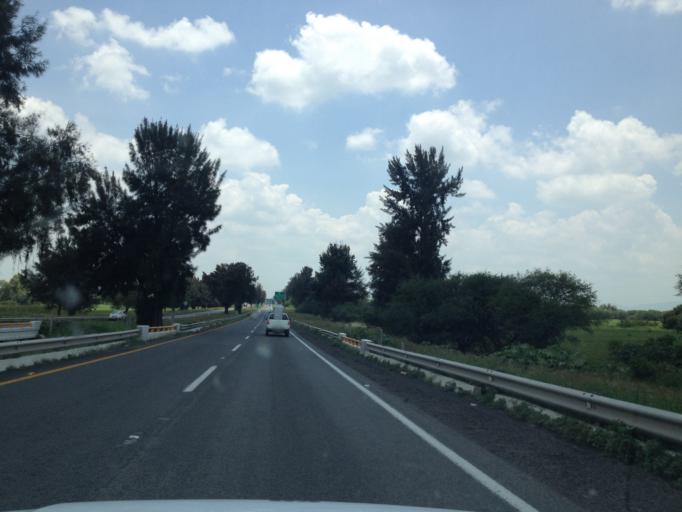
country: MX
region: Michoacan
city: Vistahermosa de Negrete
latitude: 20.2807
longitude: -102.4555
